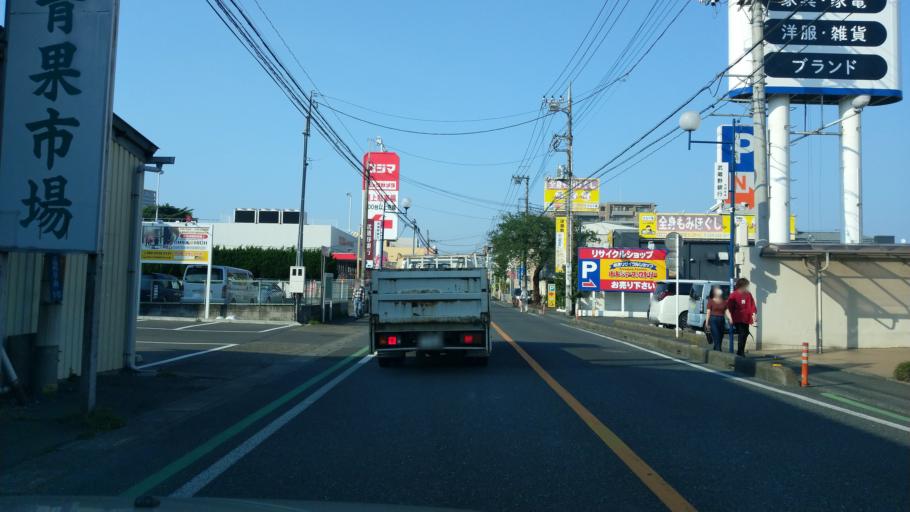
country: JP
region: Saitama
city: Kamifukuoka
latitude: 35.8666
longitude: 139.5096
